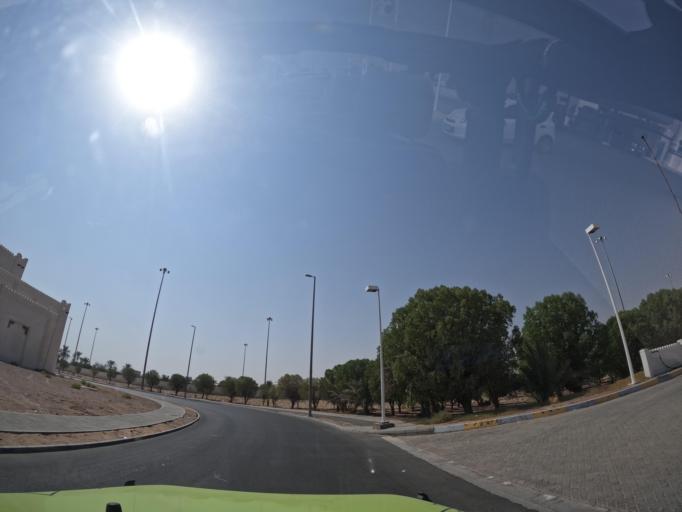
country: AE
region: Abu Dhabi
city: Al Ain
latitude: 24.2052
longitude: 55.3888
